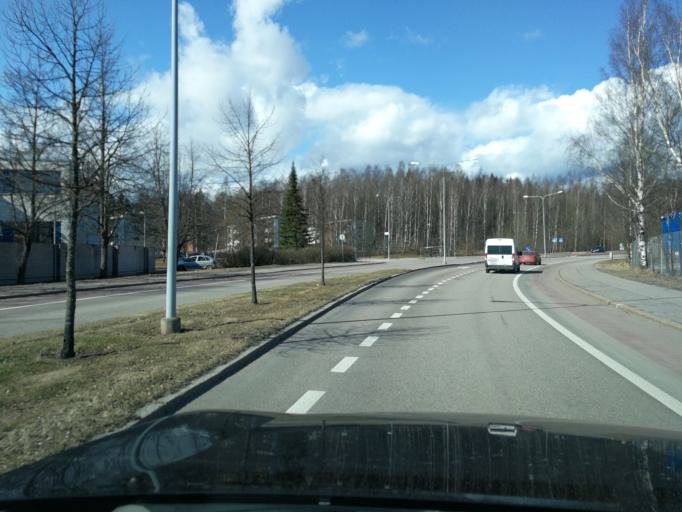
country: FI
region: Uusimaa
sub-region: Helsinki
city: Teekkarikylae
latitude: 60.2403
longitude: 24.8438
